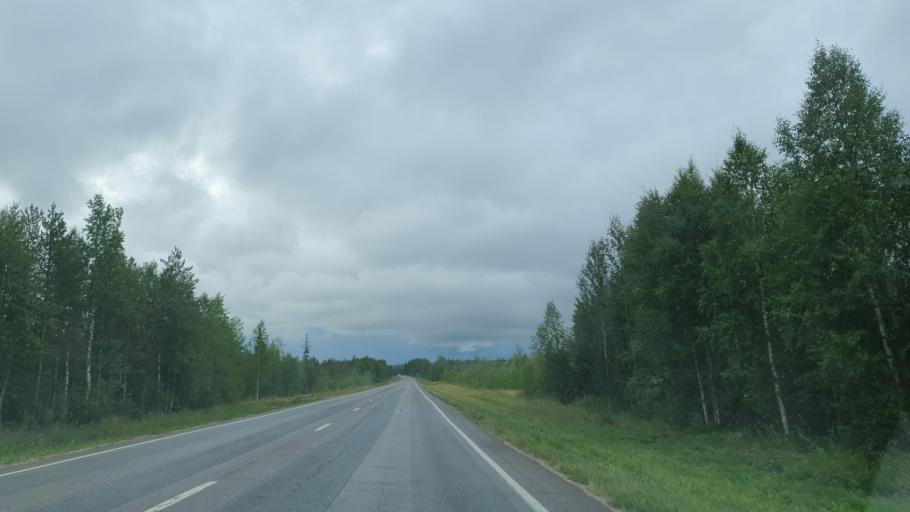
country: FI
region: Lapland
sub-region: Tunturi-Lappi
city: Kolari
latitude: 67.2179
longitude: 23.9028
